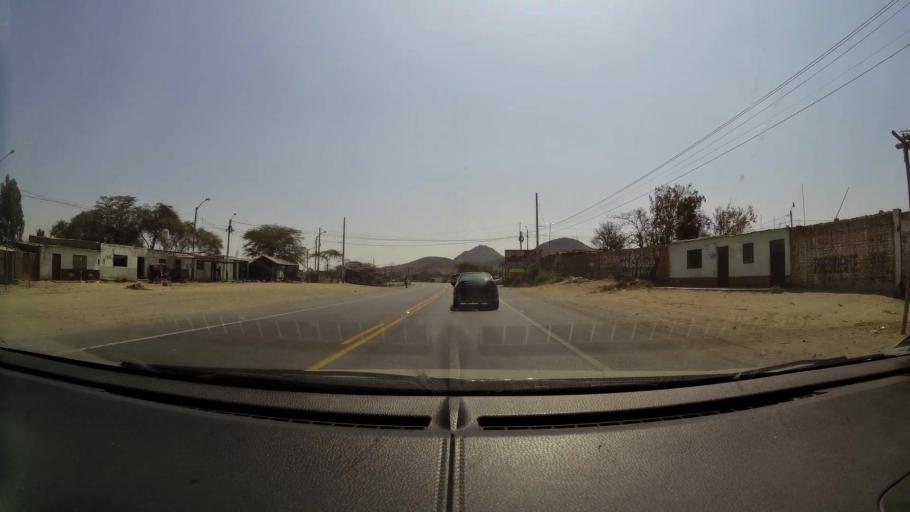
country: PE
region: Lambayeque
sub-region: Provincia de Chiclayo
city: Mocupe
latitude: -6.9793
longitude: -79.6446
